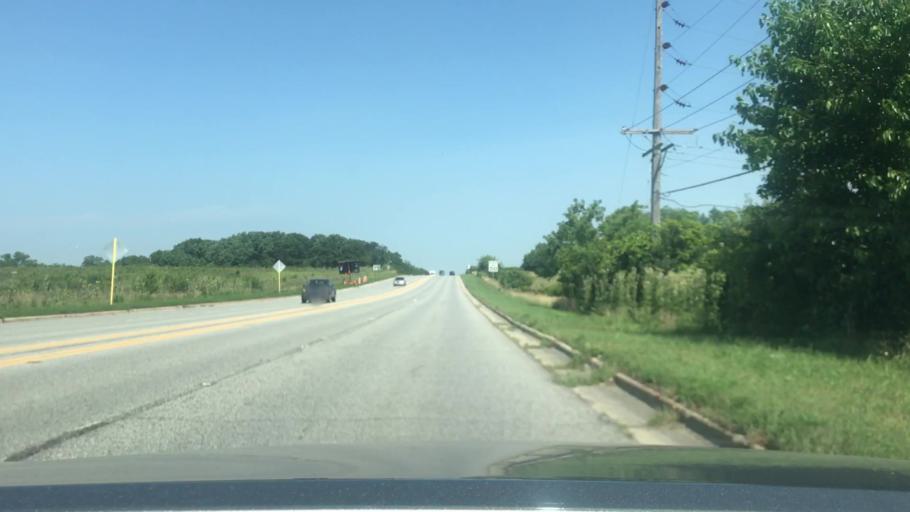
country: US
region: Illinois
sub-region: Cook County
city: Oak Forest
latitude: 41.6033
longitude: -87.7302
